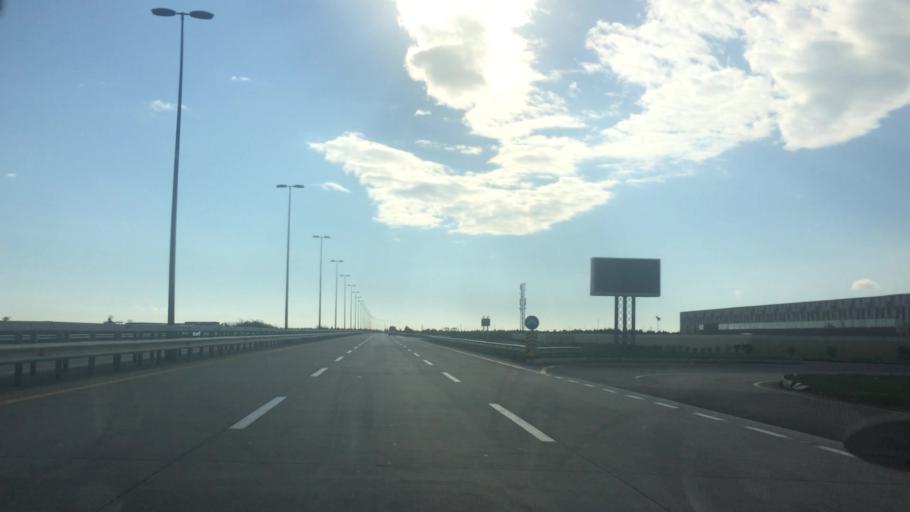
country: AZ
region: Baki
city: Hovsan
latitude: 40.3863
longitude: 50.0657
